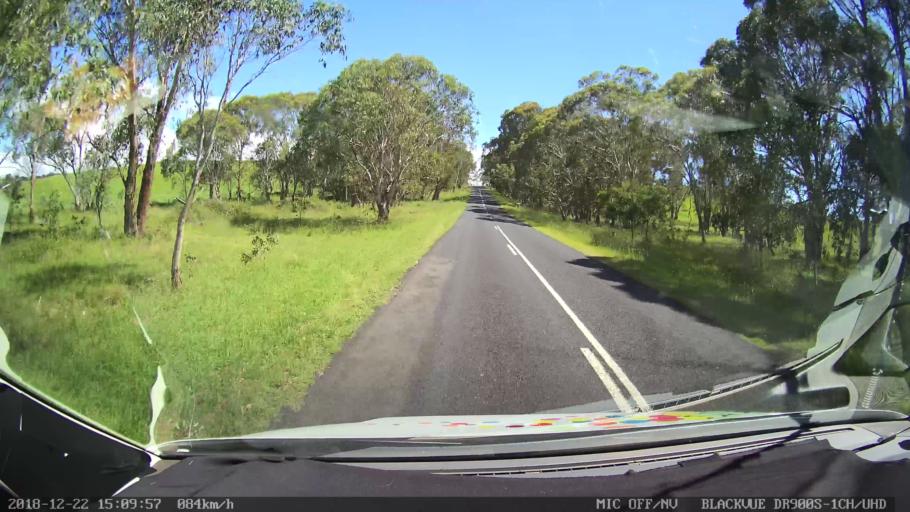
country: AU
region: New South Wales
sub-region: Bellingen
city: Dorrigo
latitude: -30.3295
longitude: 152.4058
